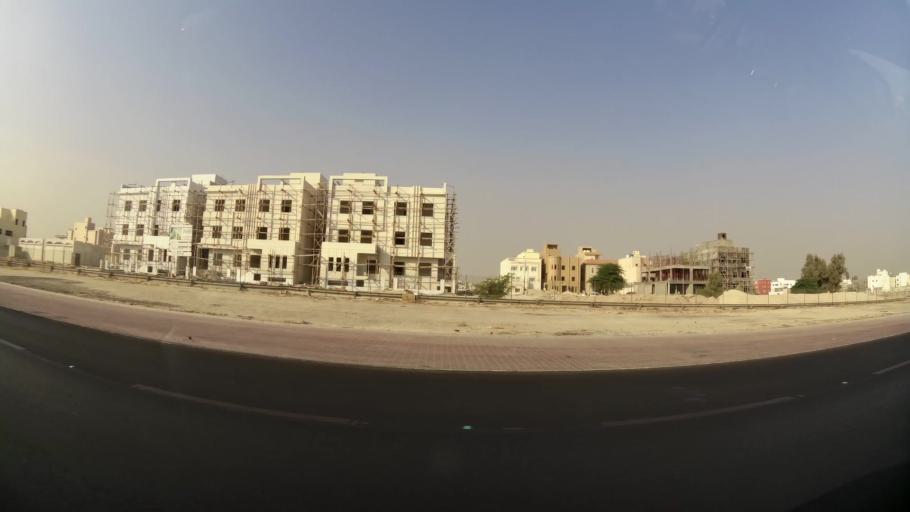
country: KW
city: Al Funaytis
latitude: 29.2252
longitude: 48.0991
